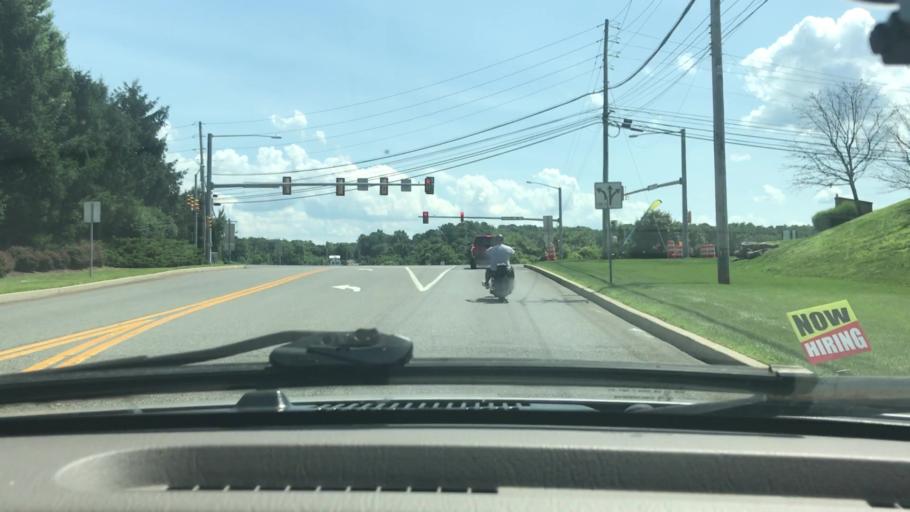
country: US
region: Pennsylvania
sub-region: Dauphin County
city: Middletown
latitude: 40.2307
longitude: -76.7379
